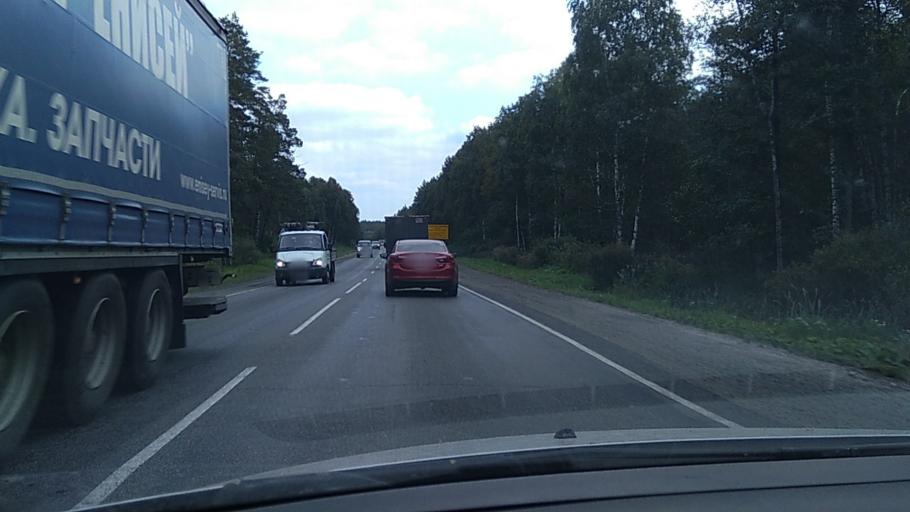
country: RU
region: Chelyabinsk
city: Miass
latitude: 54.9336
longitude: 60.1414
